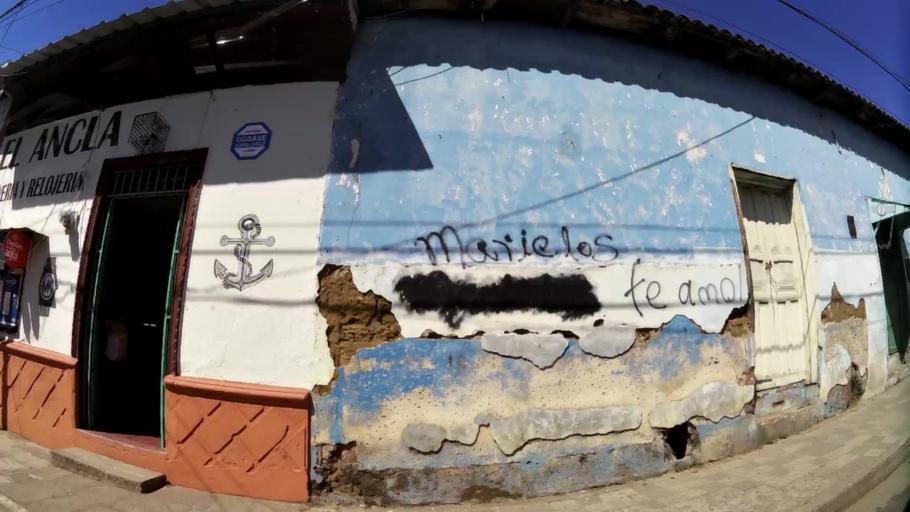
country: SV
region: Ahuachapan
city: Ahuachapan
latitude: 13.9230
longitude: -89.8453
